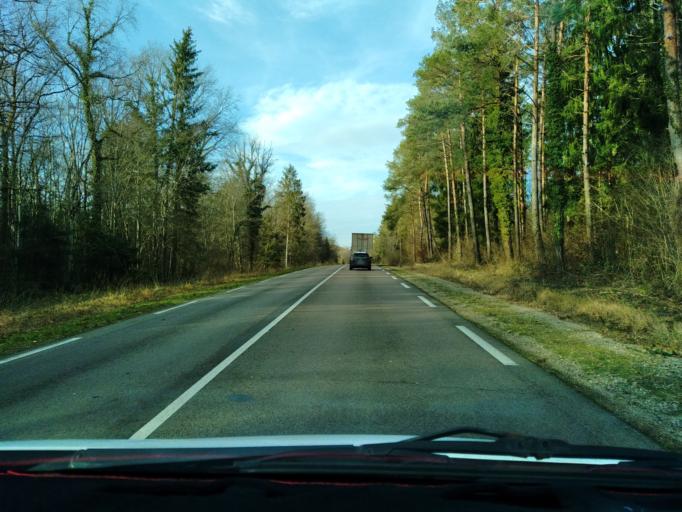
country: FR
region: Franche-Comte
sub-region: Departement de la Haute-Saone
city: Gray
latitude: 47.4017
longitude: 5.6421
